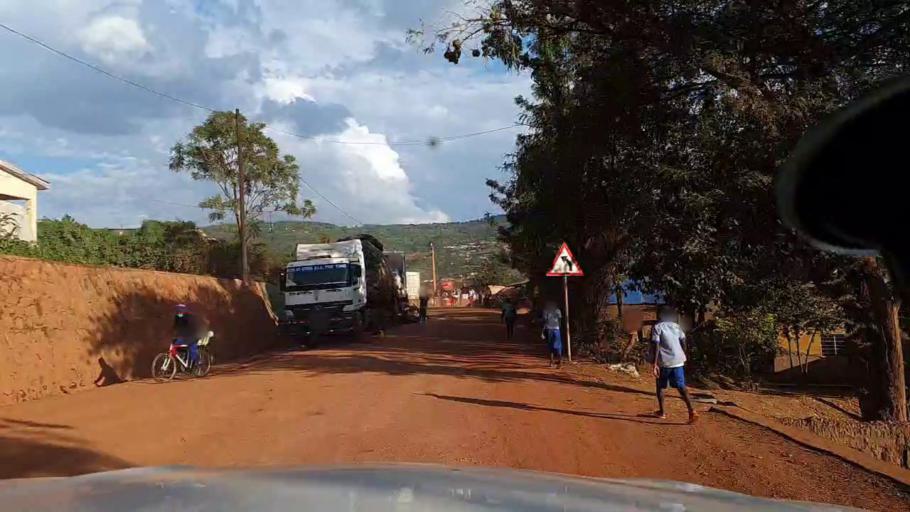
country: RW
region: Kigali
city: Kigali
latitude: -1.9466
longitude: 30.0147
